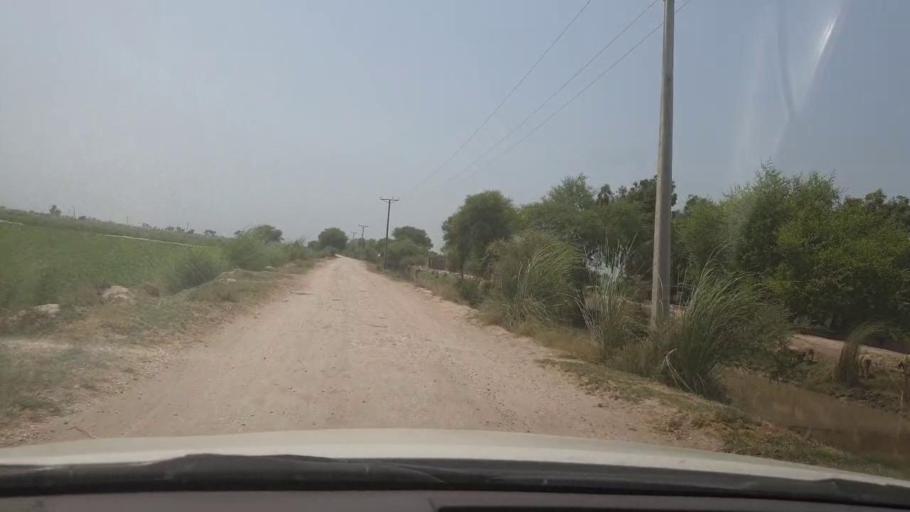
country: PK
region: Sindh
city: Shikarpur
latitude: 28.0515
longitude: 68.5921
